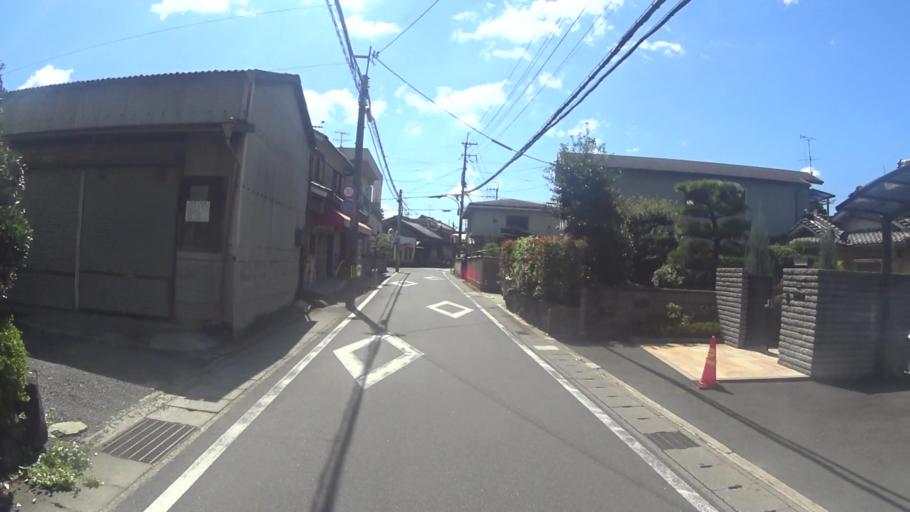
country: JP
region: Kyoto
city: Tanabe
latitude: 34.8199
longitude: 135.8072
